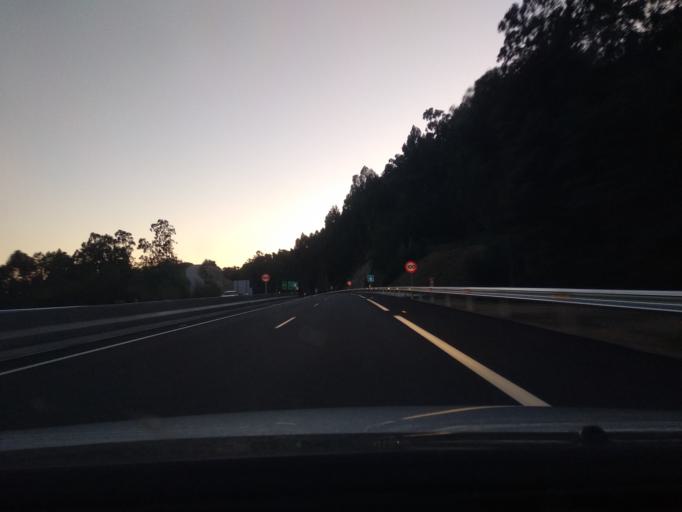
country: ES
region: Galicia
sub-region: Provincia de Pontevedra
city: Moana
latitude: 42.2962
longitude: -8.7491
